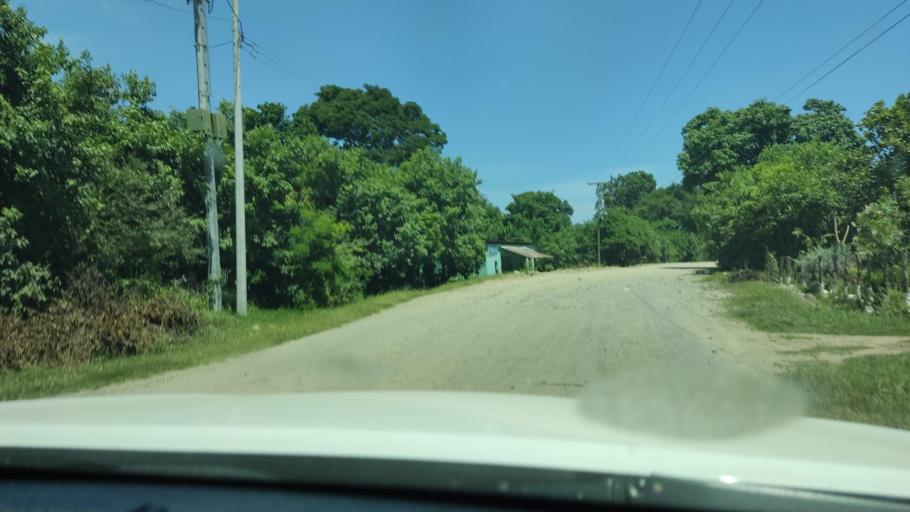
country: SV
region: Ahuachapan
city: San Francisco Menendez
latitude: 13.7763
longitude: -90.1131
